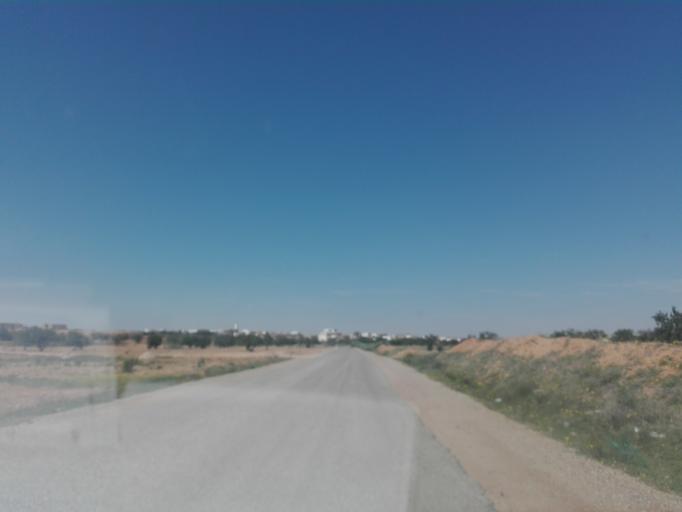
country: TN
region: Safaqis
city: Bi'r `Ali Bin Khalifah
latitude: 34.6692
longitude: 10.3584
